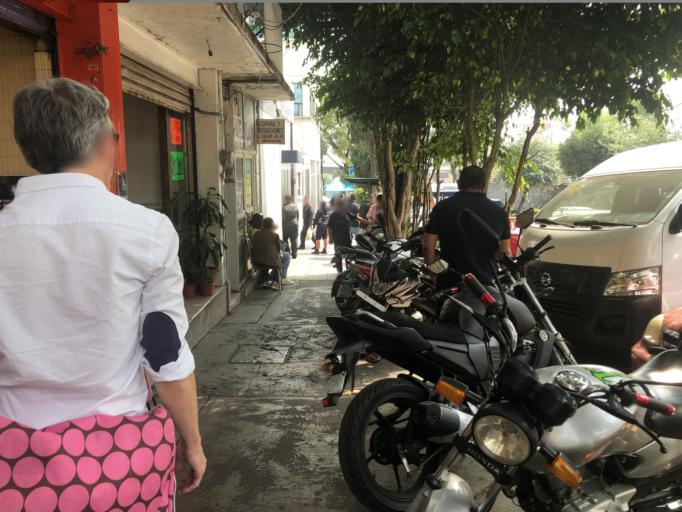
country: MX
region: Mexico
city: Naucalpan de Juarez
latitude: 19.4793
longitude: -99.2333
